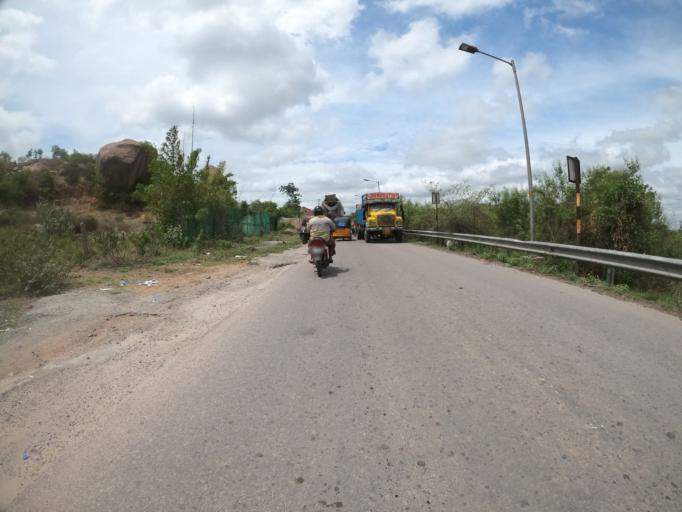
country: IN
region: Telangana
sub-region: Hyderabad
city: Hyderabad
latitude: 17.3143
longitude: 78.3722
